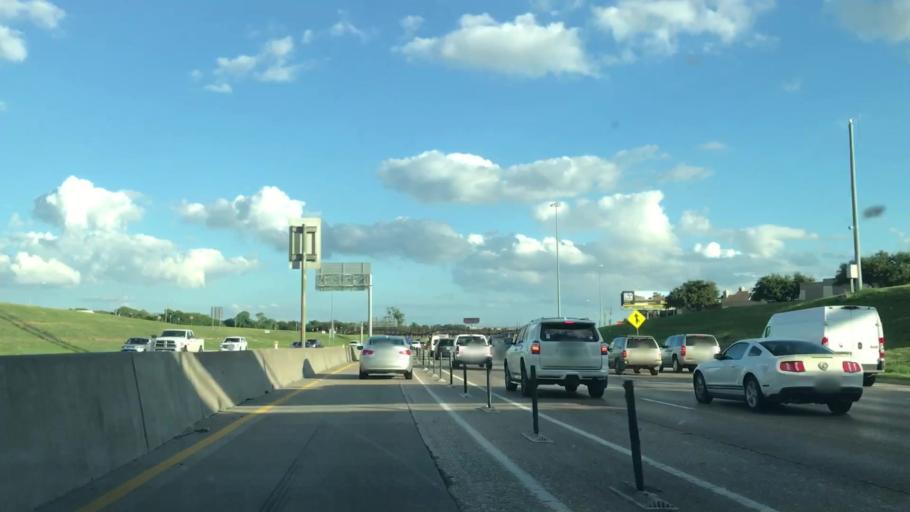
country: US
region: Texas
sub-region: Dallas County
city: Richardson
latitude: 32.9002
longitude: -96.7175
